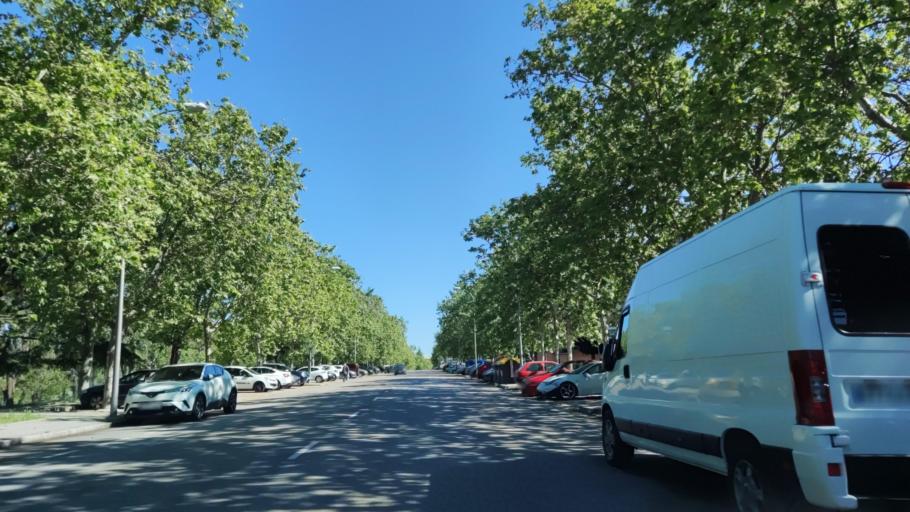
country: ES
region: Madrid
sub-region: Provincia de Madrid
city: San Blas
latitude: 40.4296
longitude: -3.6203
